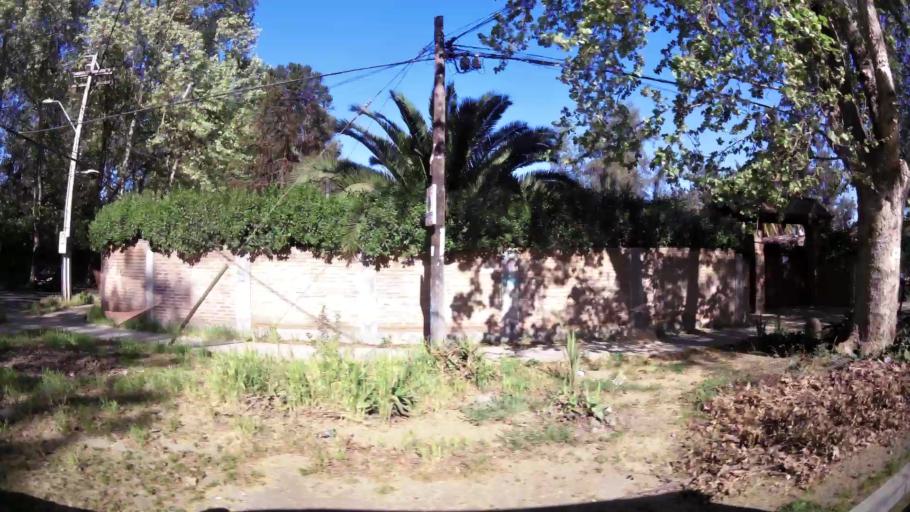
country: CL
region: Santiago Metropolitan
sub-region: Provincia de Talagante
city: Penaflor
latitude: -33.6002
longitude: -70.8674
